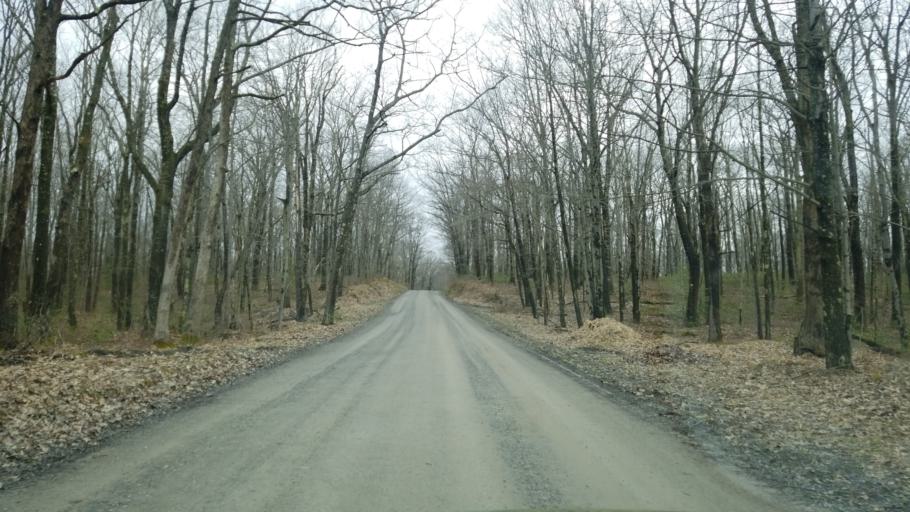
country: US
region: Pennsylvania
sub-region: Clearfield County
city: Shiloh
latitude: 41.1679
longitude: -78.3410
